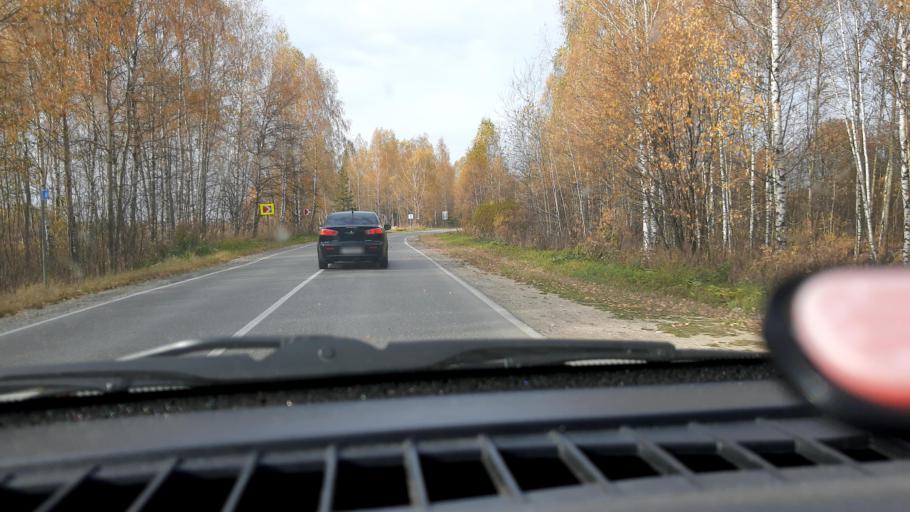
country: RU
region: Nizjnij Novgorod
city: Neklyudovo
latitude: 56.5037
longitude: 43.8470
